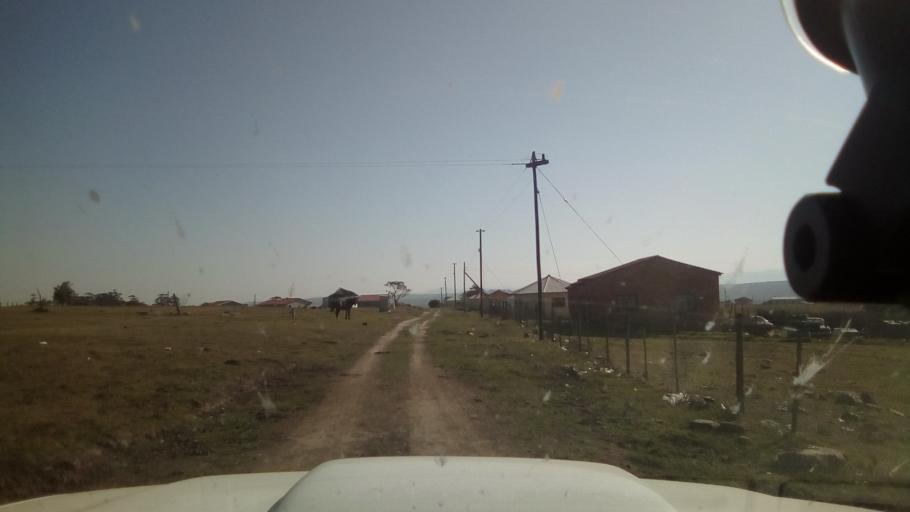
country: ZA
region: Eastern Cape
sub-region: Buffalo City Metropolitan Municipality
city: Bhisho
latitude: -32.9393
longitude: 27.3398
